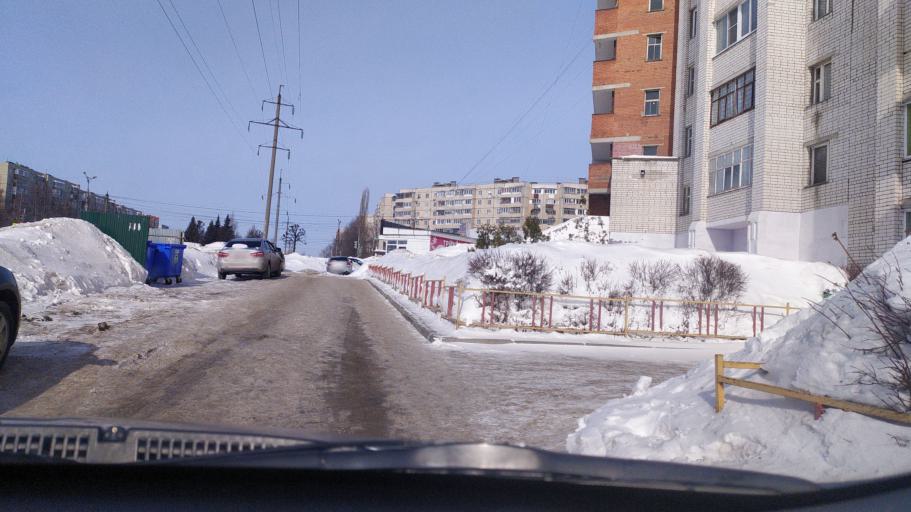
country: RU
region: Chuvashia
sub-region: Cheboksarskiy Rayon
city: Cheboksary
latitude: 56.0998
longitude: 47.3020
